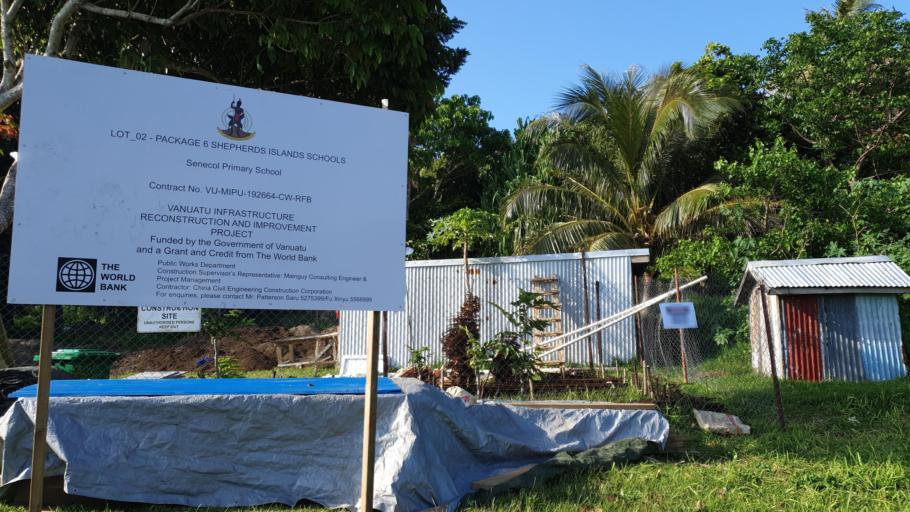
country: VU
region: Shefa
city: Port-Vila
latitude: -17.0225
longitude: 168.5886
